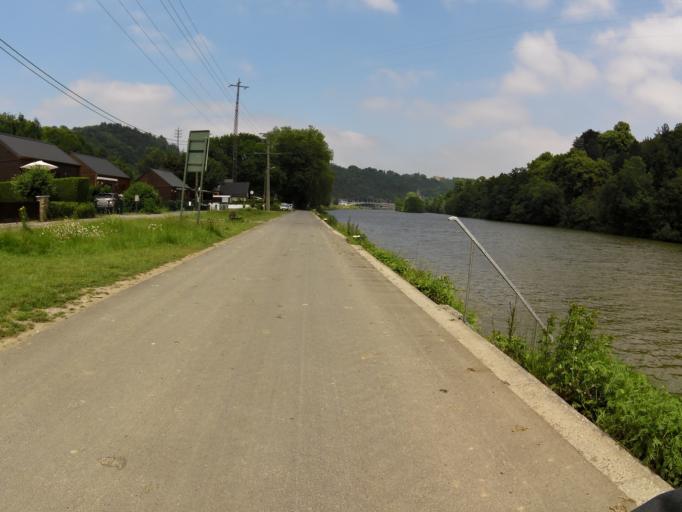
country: BE
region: Wallonia
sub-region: Province de Namur
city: Hastiere-Lavaux
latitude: 50.2087
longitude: 4.8207
